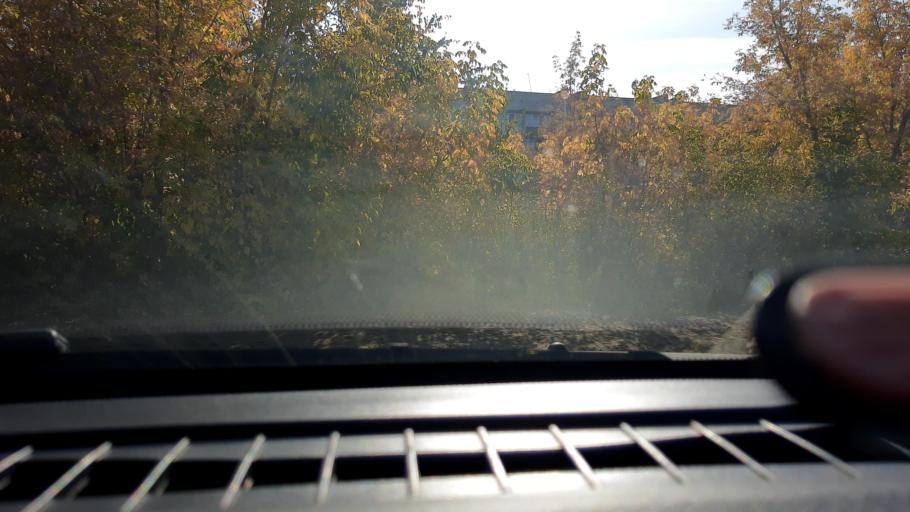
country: RU
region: Nizjnij Novgorod
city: Burevestnik
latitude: 56.2041
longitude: 43.8095
